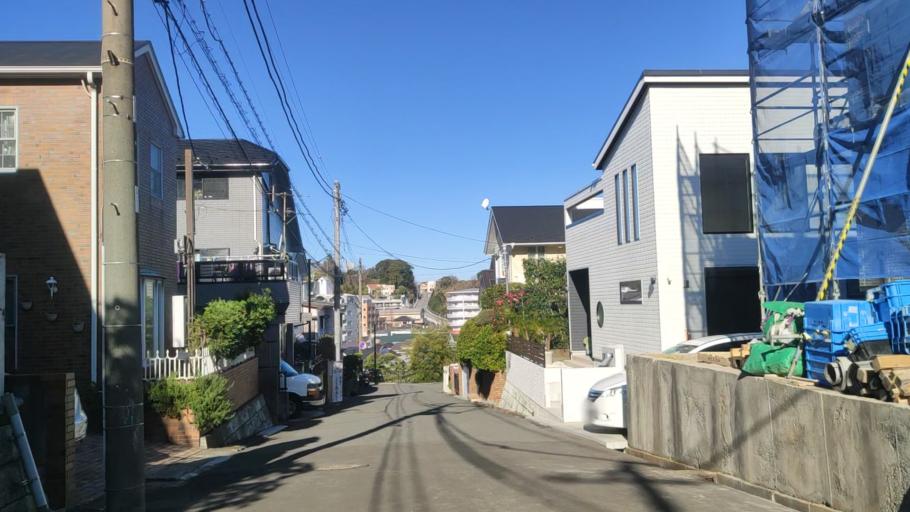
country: JP
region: Kanagawa
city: Yokohama
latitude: 35.4191
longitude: 139.6579
